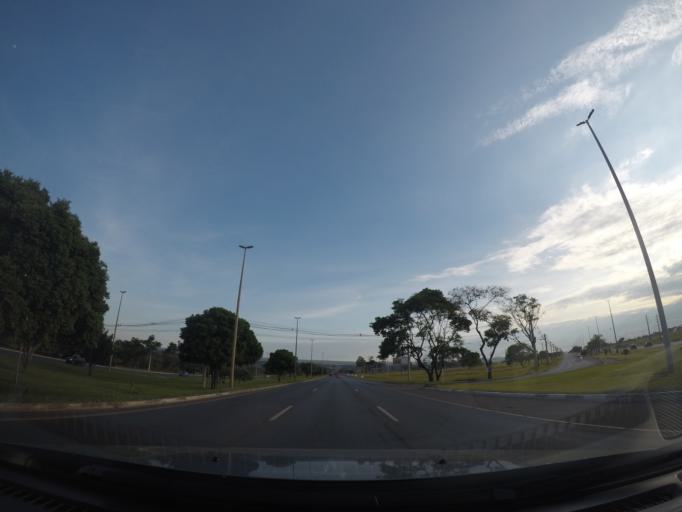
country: BR
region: Federal District
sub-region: Brasilia
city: Brasilia
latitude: -15.7393
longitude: -47.9162
